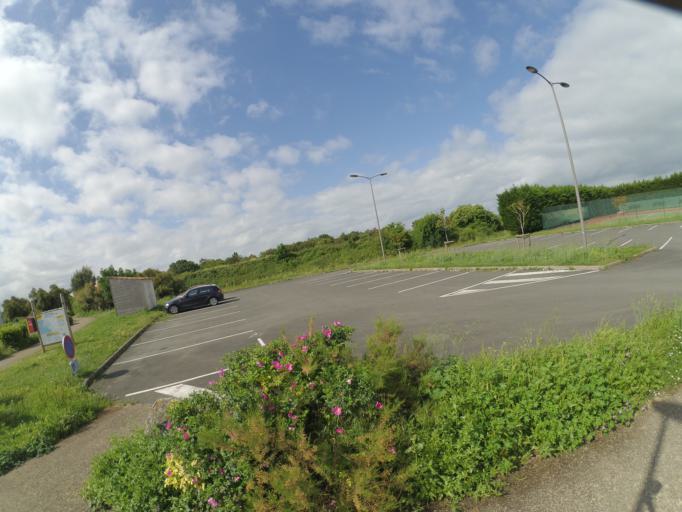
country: FR
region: Poitou-Charentes
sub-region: Departement de la Charente-Maritime
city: Angoulins
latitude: 46.1078
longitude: -1.1161
